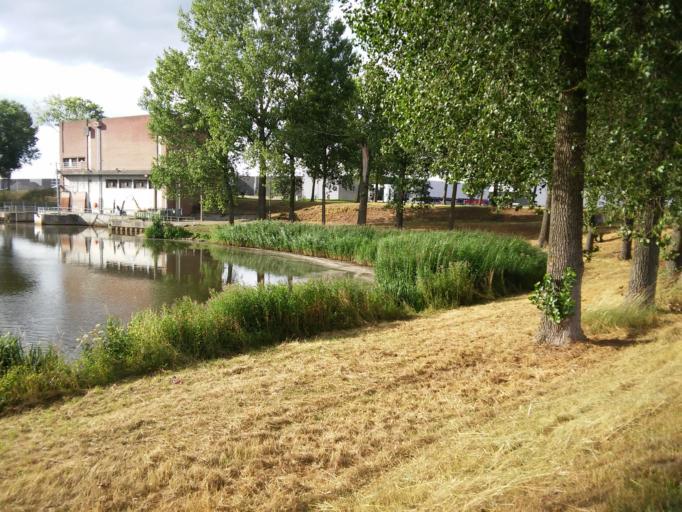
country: BE
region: Flanders
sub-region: Provincie Antwerpen
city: Niel
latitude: 51.0954
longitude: 4.3199
